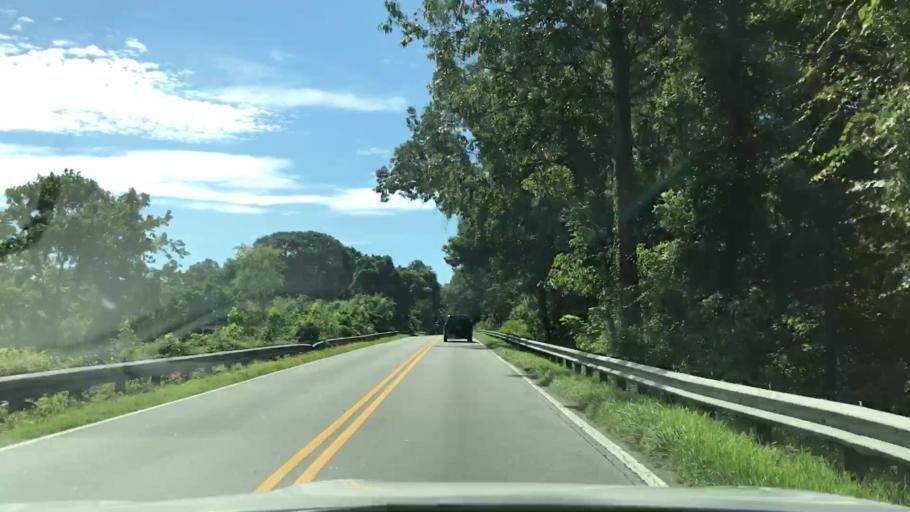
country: US
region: South Carolina
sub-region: Charleston County
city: Shell Point
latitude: 32.8428
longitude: -80.0573
